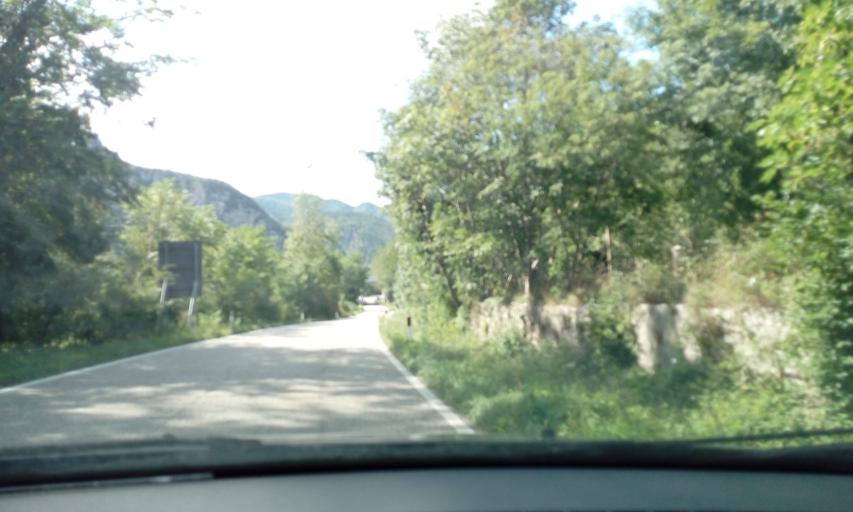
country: IT
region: Friuli Venezia Giulia
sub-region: Provincia di Udine
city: Trasaghis
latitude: 46.2834
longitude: 13.0680
